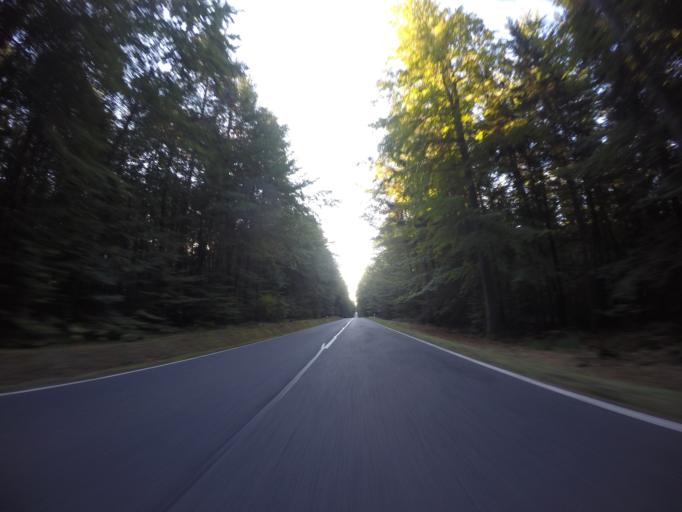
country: DE
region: Bavaria
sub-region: Regierungsbezirk Unterfranken
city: Schollbrunn
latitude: 49.8500
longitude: 9.4407
